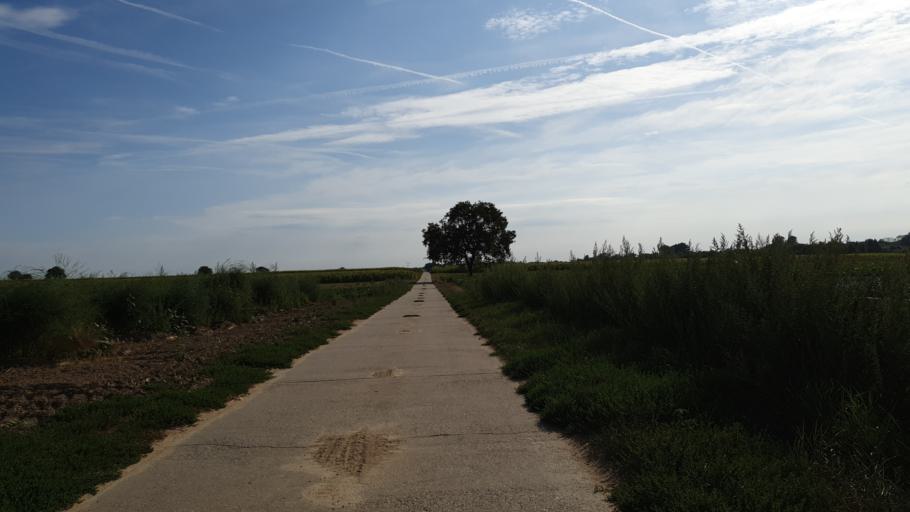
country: DE
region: Rheinland-Pfalz
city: Winden
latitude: 49.1053
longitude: 8.1045
